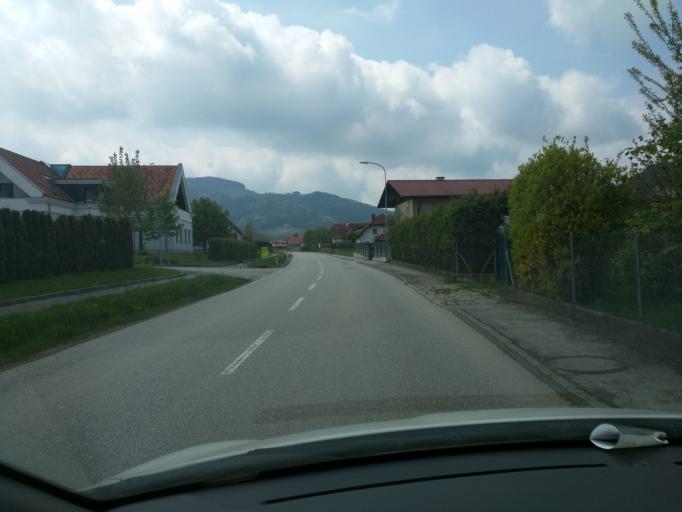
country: AT
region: Lower Austria
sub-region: Politischer Bezirk Scheibbs
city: Wang
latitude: 48.0435
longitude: 15.0243
